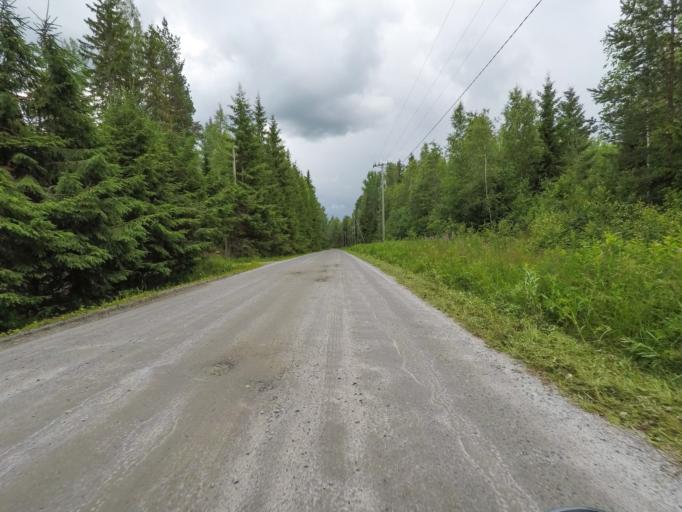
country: FI
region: Central Finland
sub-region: Jyvaeskylae
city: Hankasalmi
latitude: 62.4294
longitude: 26.6458
